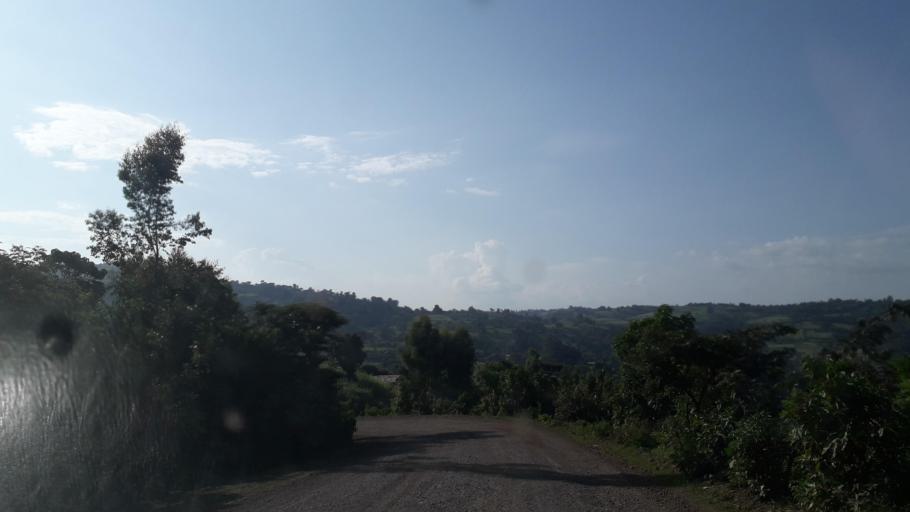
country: ET
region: Oromiya
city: Jima
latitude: 7.4720
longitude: 36.8785
